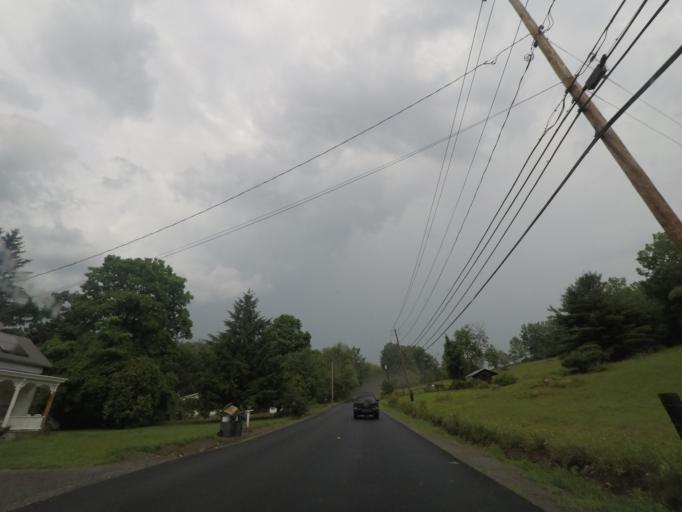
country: US
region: New York
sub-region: Rensselaer County
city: Poestenkill
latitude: 42.6890
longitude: -73.5448
